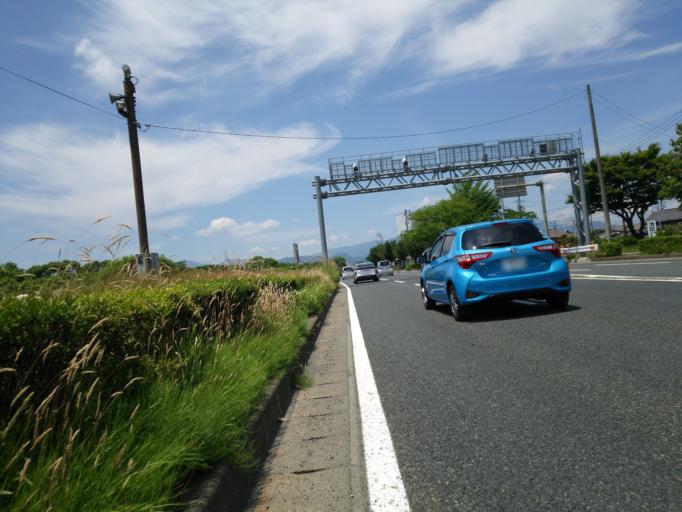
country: JP
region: Iwate
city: Morioka-shi
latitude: 39.7041
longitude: 141.1238
